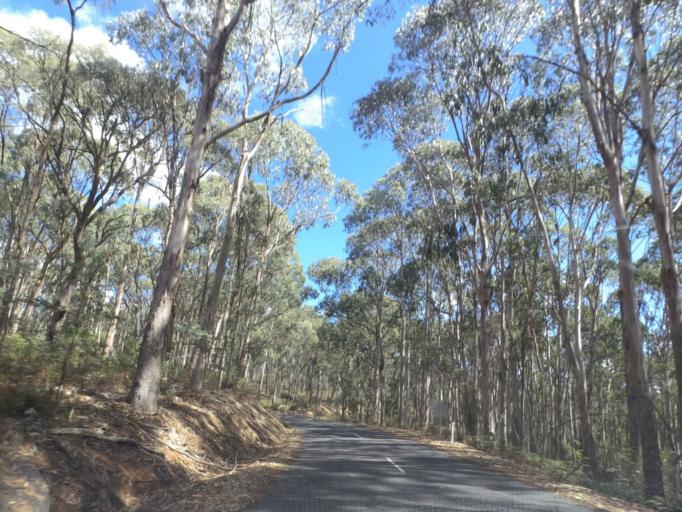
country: AU
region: Victoria
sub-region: Murrindindi
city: Alexandra
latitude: -37.3354
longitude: 145.9616
